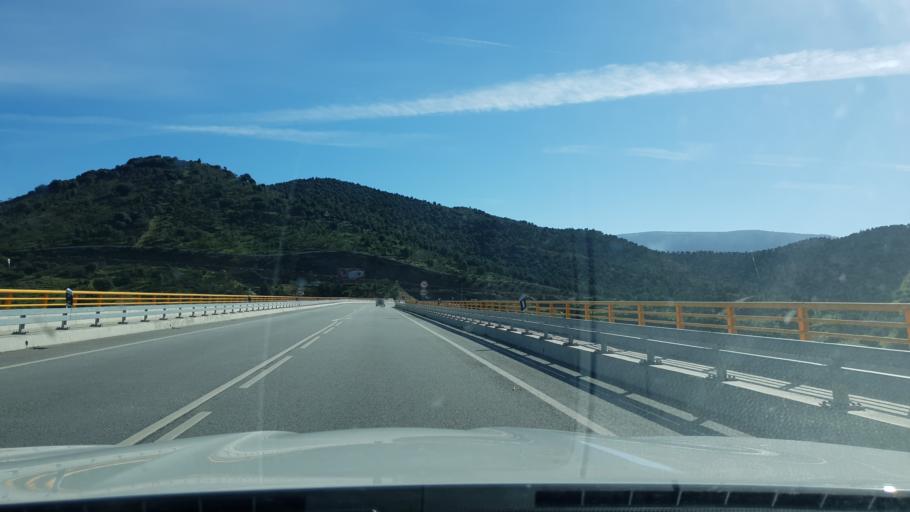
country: PT
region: Braganca
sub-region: Torre de Moncorvo
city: Torre de Moncorvo
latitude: 41.2102
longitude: -7.0842
